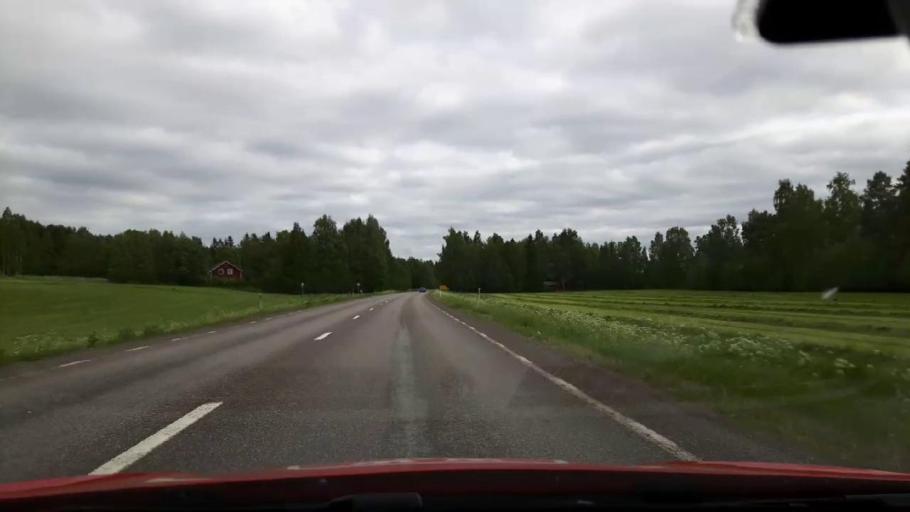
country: SE
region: Jaemtland
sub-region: Ragunda Kommun
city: Hammarstrand
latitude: 63.1307
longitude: 16.3520
